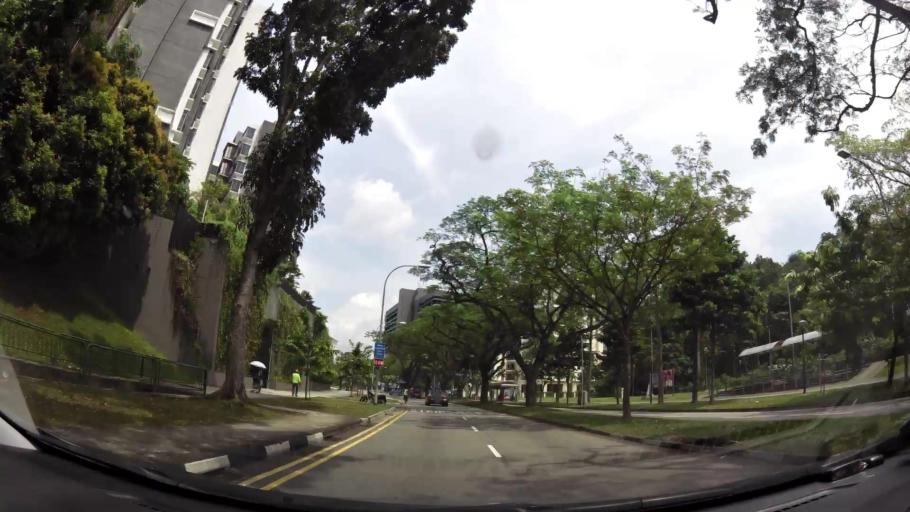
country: SG
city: Singapore
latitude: 1.3553
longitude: 103.7616
